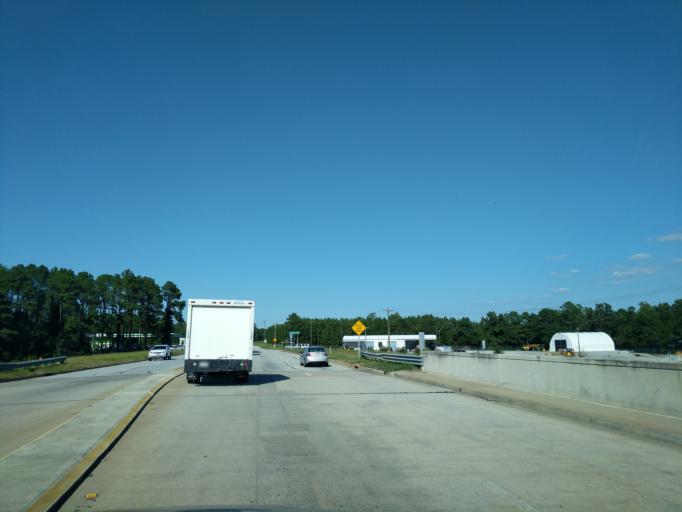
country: US
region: South Carolina
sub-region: Laurens County
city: Clinton
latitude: 34.4968
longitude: -81.8441
